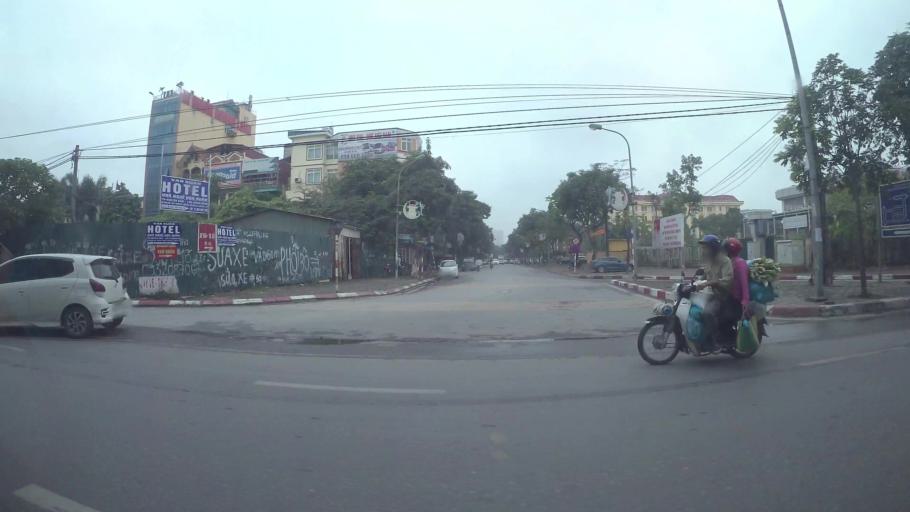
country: VN
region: Ha Noi
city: Van Dien
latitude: 20.9660
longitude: 105.8449
